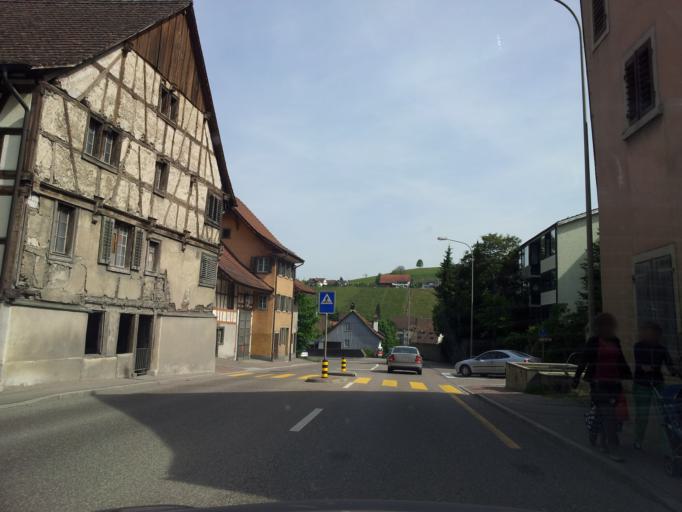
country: CH
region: Zurich
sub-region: Bezirk Buelach
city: Seglingen
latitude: 47.5728
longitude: 8.5231
